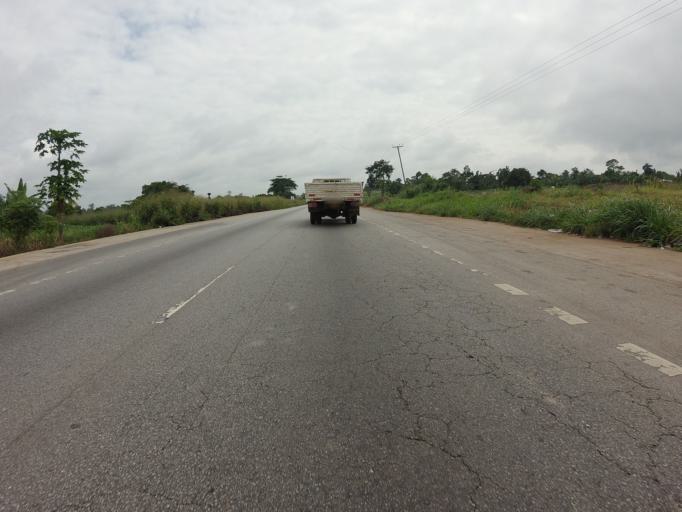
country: GH
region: Ashanti
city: Tafo
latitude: 6.9816
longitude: -1.6875
